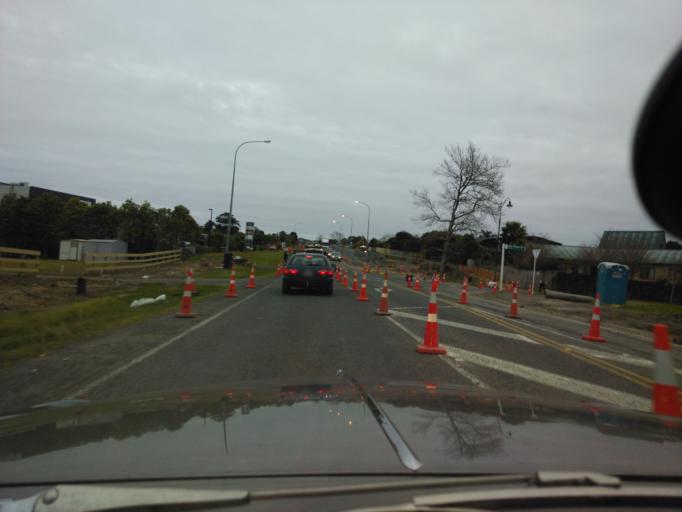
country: NZ
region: Auckland
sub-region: Auckland
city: Rothesay Bay
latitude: -36.7455
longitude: 174.6932
